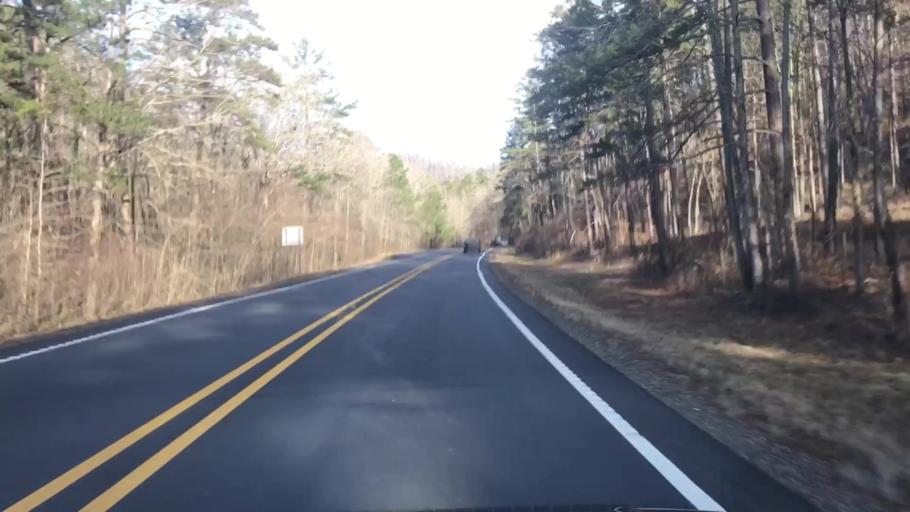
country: US
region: Arkansas
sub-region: Montgomery County
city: Mount Ida
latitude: 34.5204
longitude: -93.3894
